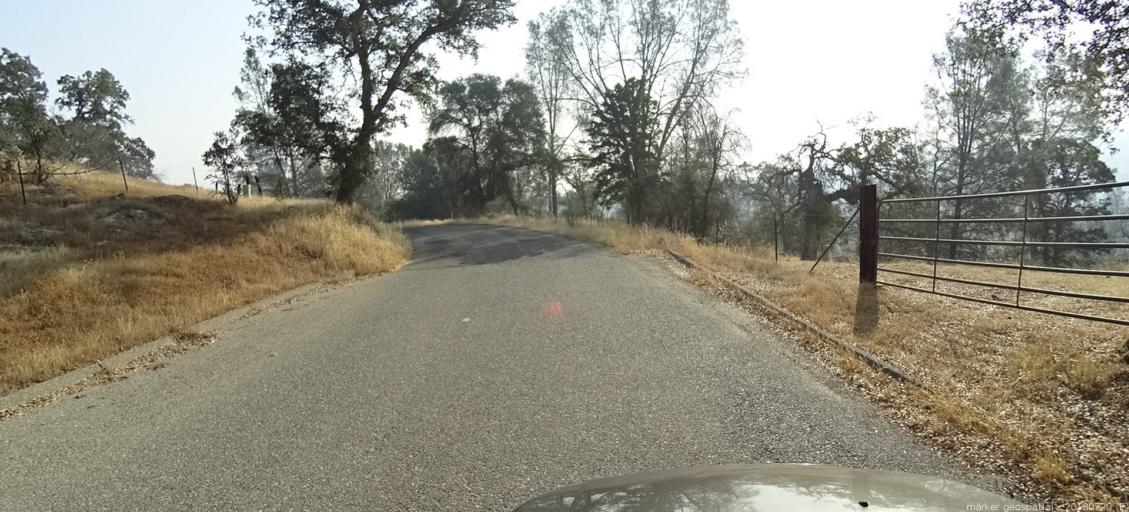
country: US
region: California
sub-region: Madera County
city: Yosemite Lakes
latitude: 37.2913
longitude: -119.8660
